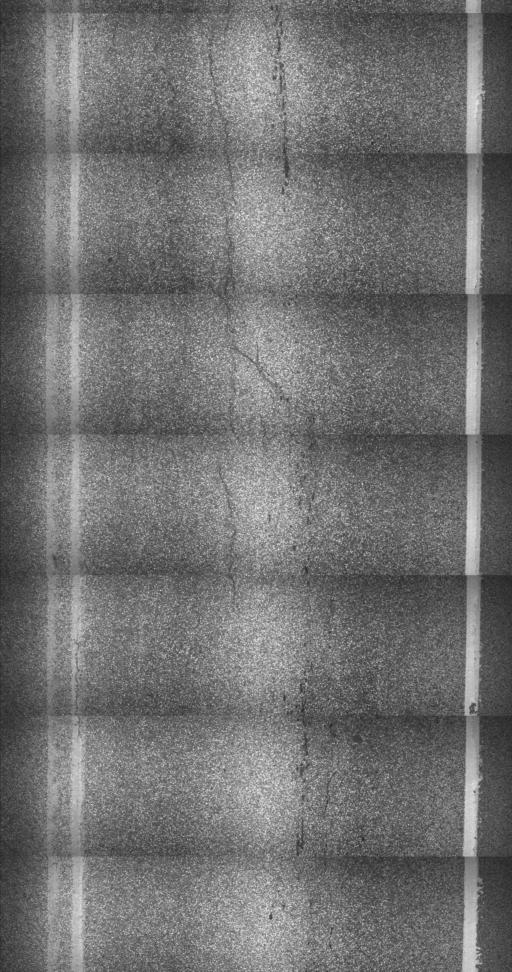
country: US
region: Vermont
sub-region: Washington County
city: Barre
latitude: 44.2836
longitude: -72.4689
